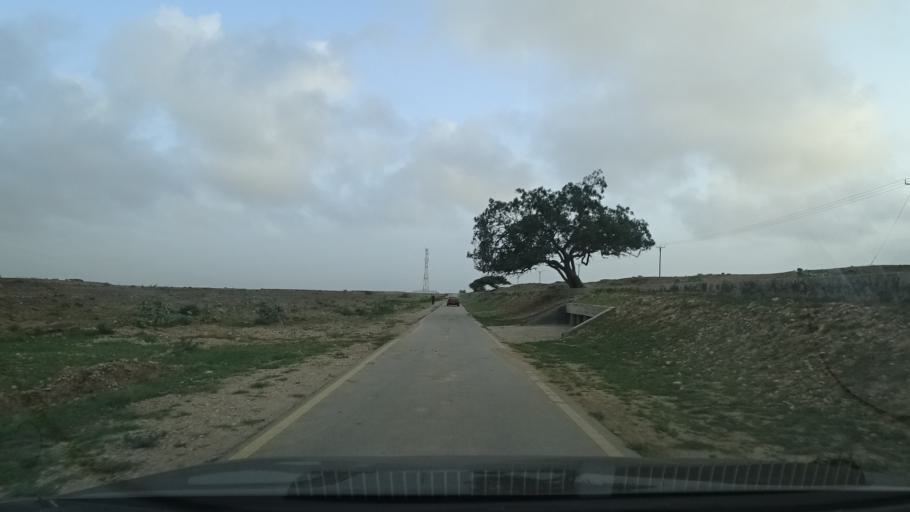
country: OM
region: Zufar
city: Salalah
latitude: 17.0909
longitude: 54.2329
